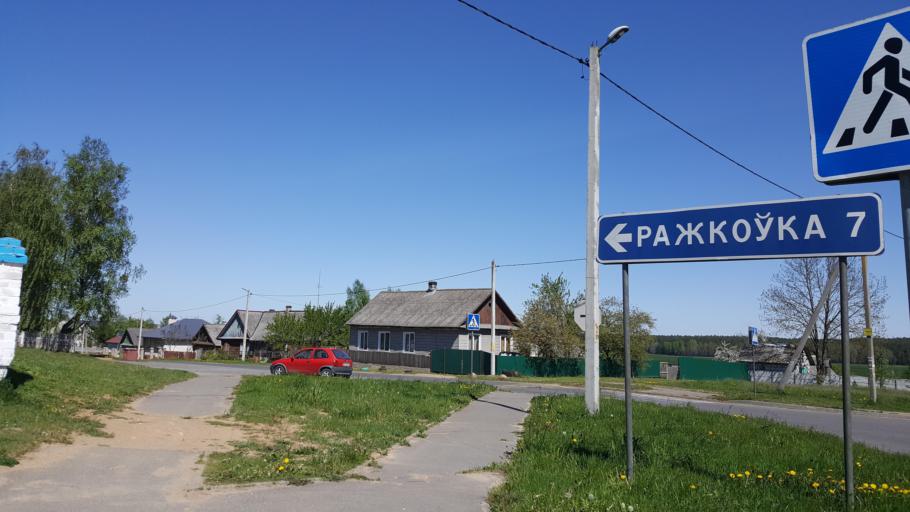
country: BY
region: Brest
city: Kamyanyuki
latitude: 52.4916
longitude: 23.7785
